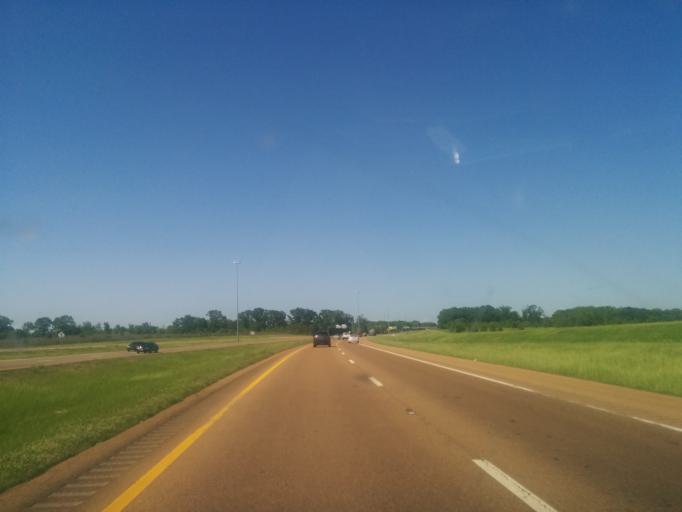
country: US
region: Mississippi
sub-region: Madison County
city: Madison
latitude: 32.5406
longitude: -90.0947
